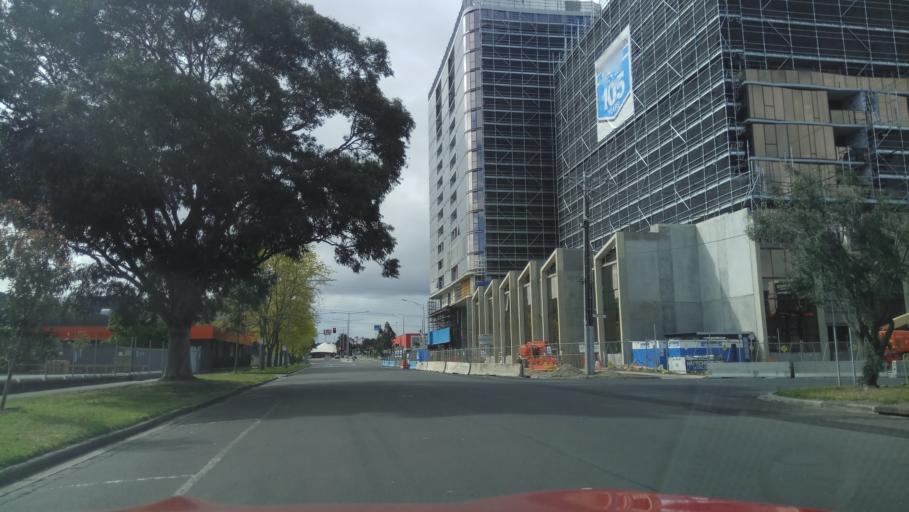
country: AU
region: Victoria
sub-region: Port Phillip
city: Port Melbourne
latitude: -37.8352
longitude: 144.9196
